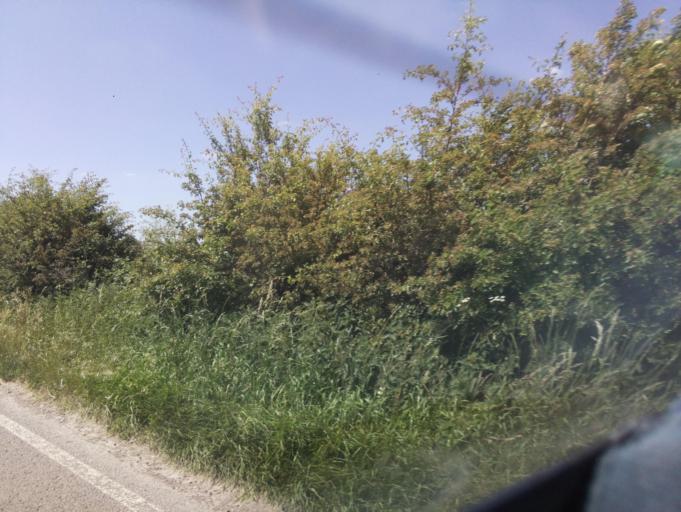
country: GB
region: England
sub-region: Wiltshire
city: Lydiard Tregoze
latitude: 51.5381
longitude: -1.8355
